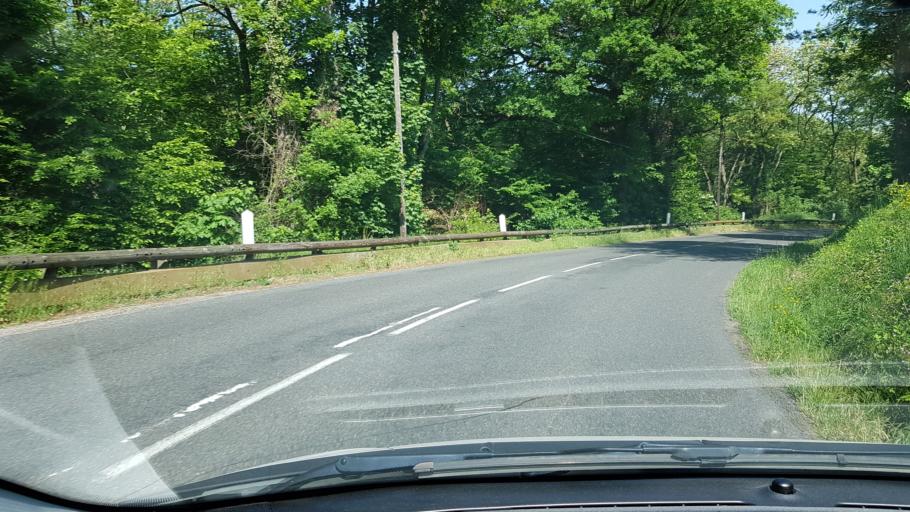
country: FR
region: Rhone-Alpes
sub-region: Departement du Rhone
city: Orlienas
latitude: 45.6606
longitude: 4.7217
